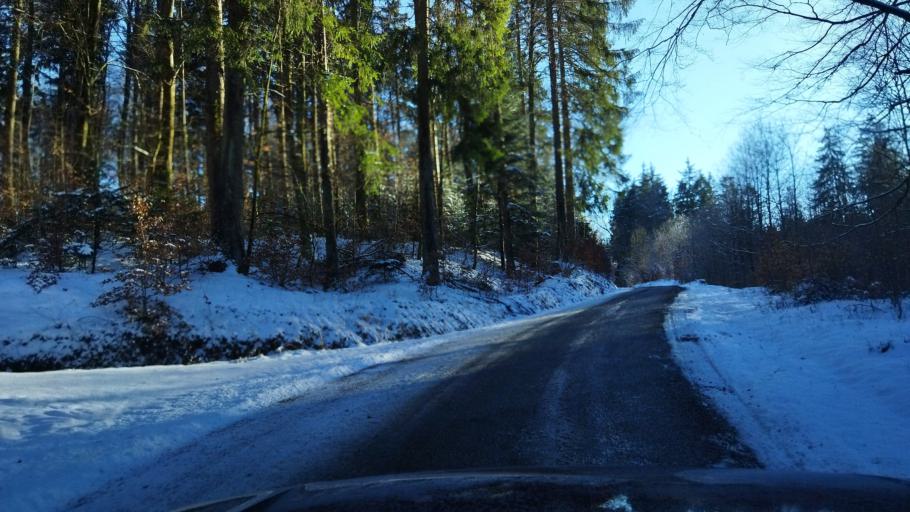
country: DE
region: Baden-Wuerttemberg
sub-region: Regierungsbezirk Stuttgart
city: Gerabronn
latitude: 48.9674
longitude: 9.9186
